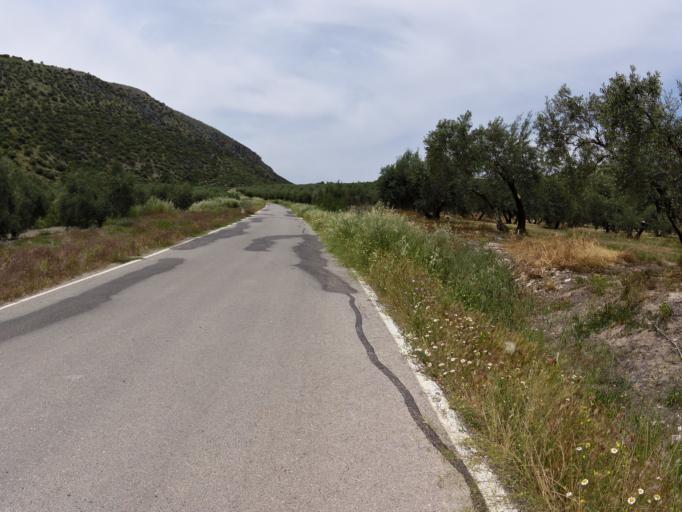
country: ES
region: Andalusia
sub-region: Province of Cordoba
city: Luque
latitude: 37.5193
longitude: -4.2230
